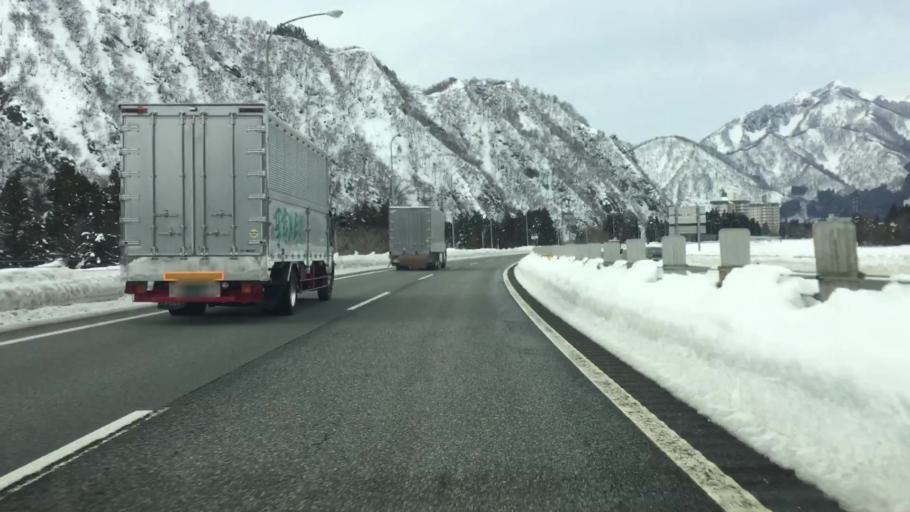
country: JP
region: Niigata
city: Shiozawa
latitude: 36.9098
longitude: 138.8407
